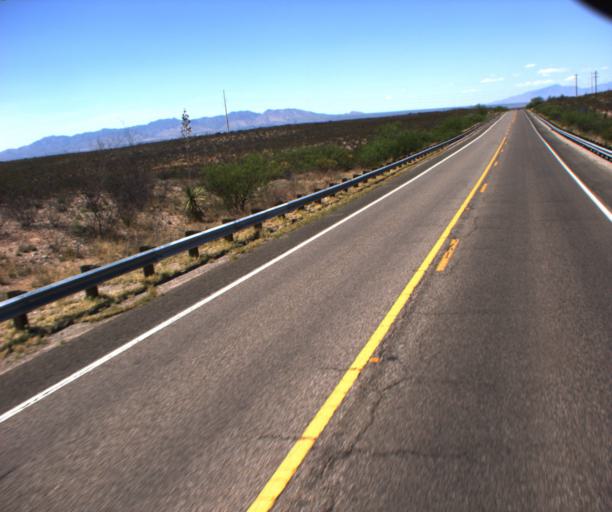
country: US
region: Arizona
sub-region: Cochise County
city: Tombstone
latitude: 31.7710
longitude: -110.1250
